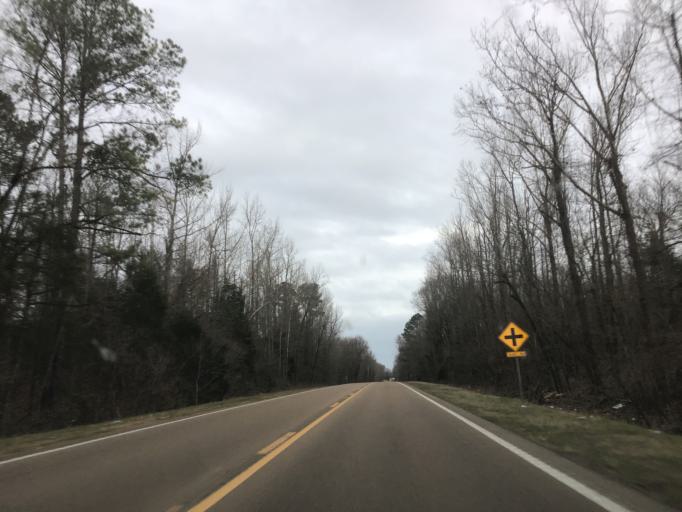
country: US
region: Mississippi
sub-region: Warren County
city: Beechwood
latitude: 32.3064
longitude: -90.8035
